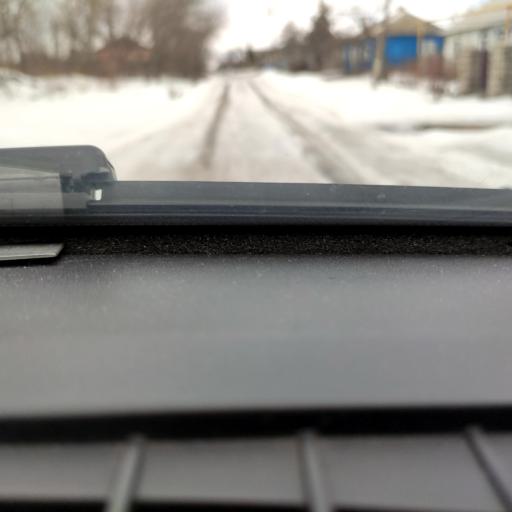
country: RU
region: Voronezj
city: Strelitsa
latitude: 51.6049
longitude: 38.9121
